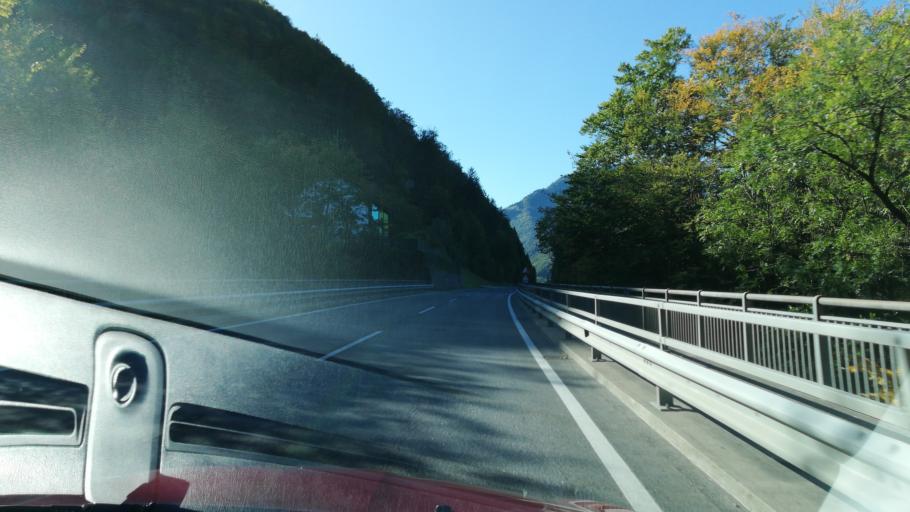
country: AT
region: Upper Austria
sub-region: Politischer Bezirk Steyr-Land
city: Weyer
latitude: 47.8220
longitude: 14.6455
